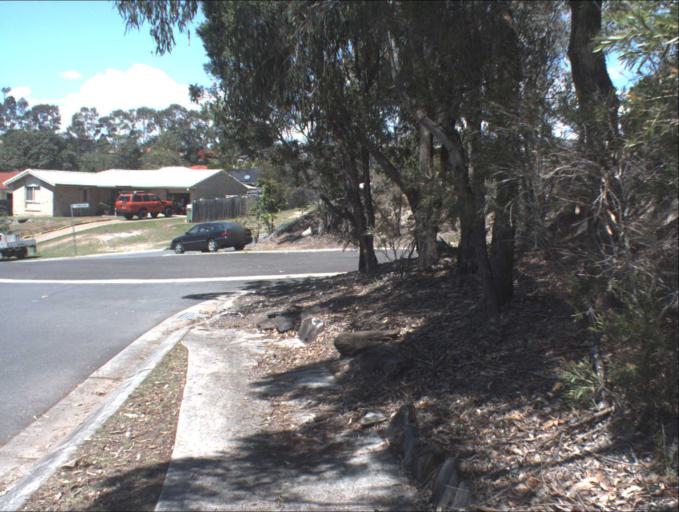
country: AU
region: Queensland
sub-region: Logan
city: Waterford West
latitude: -27.7066
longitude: 153.1664
